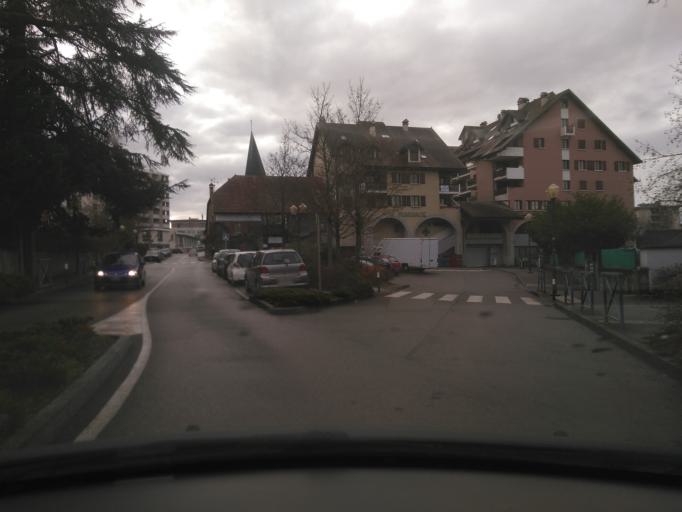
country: FR
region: Rhone-Alpes
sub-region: Departement de la Haute-Savoie
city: Saint-Julien-en-Genevois
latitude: 46.1456
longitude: 6.0807
